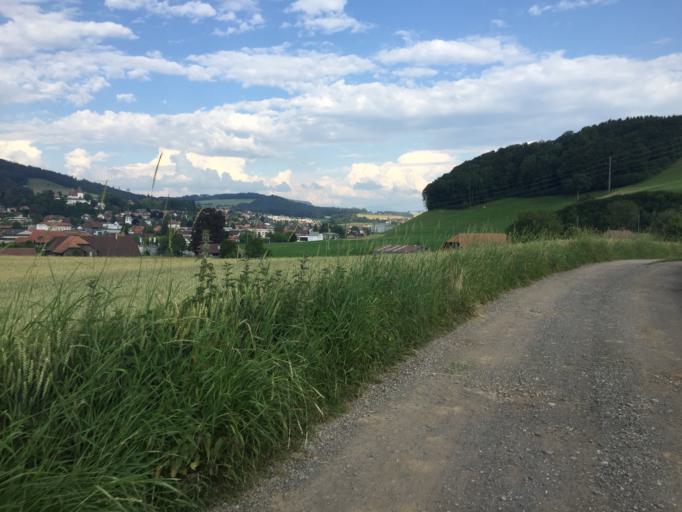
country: CH
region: Bern
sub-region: Bern-Mittelland District
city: Worb
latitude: 46.9297
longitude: 7.5508
